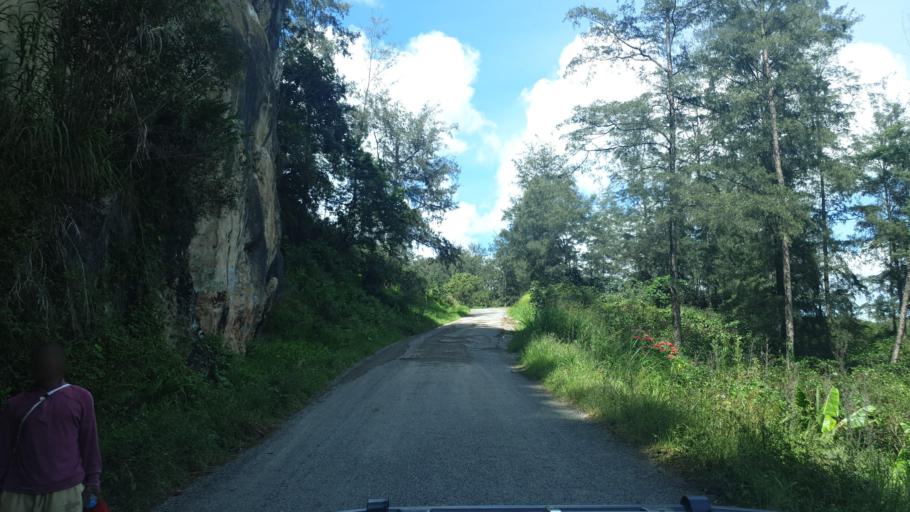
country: PG
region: Chimbu
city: Kundiawa
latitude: -6.1503
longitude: 145.1336
